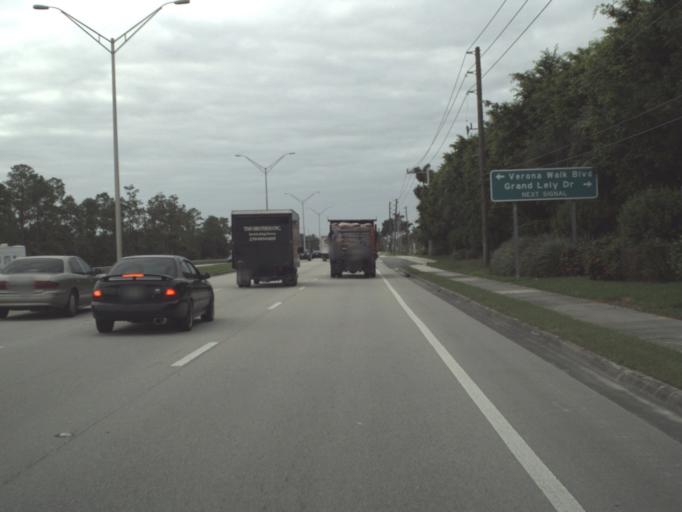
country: US
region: Florida
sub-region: Collier County
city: Lely Resort
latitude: 26.0917
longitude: -81.6874
